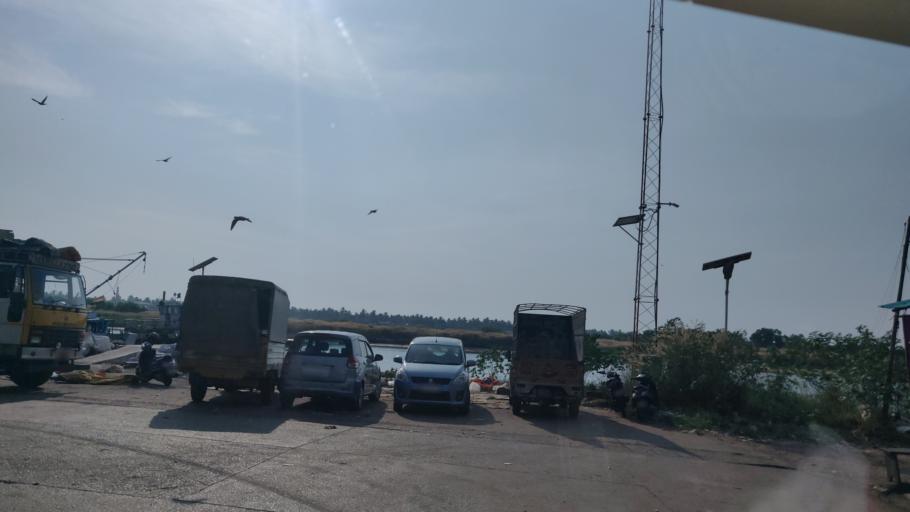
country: IN
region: Karnataka
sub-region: Dakshina Kannada
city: Mangalore
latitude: 12.8654
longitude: 74.8313
